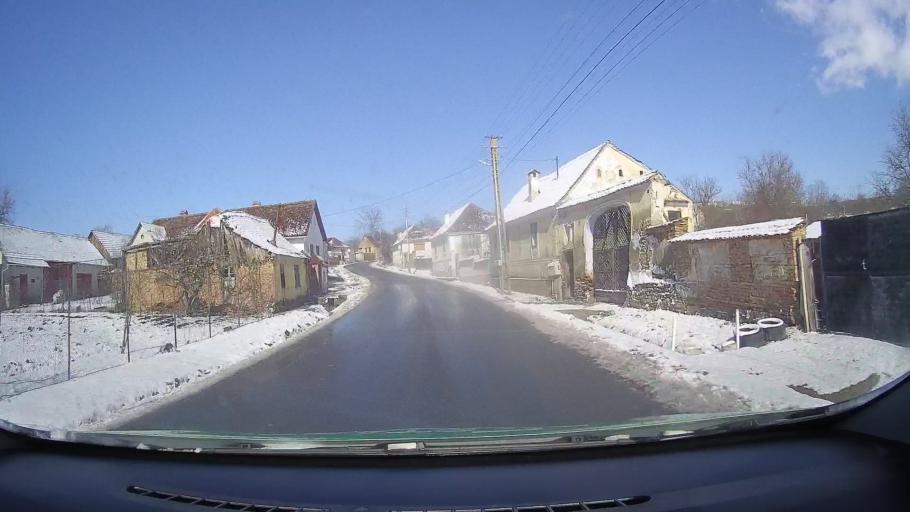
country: RO
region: Sibiu
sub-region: Comuna Avrig
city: Avrig
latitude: 45.7626
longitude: 24.3875
